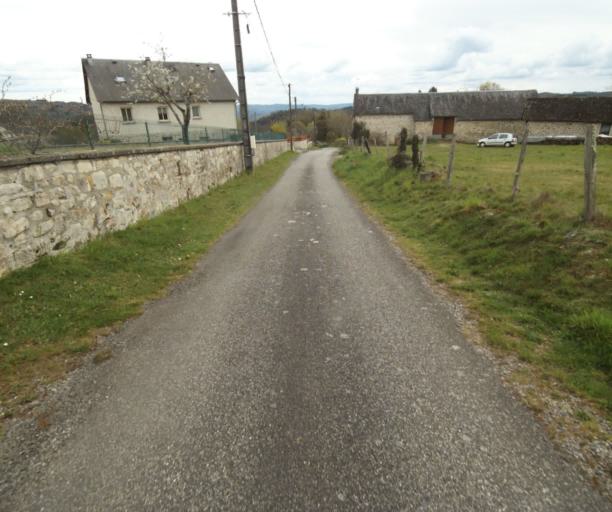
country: FR
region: Limousin
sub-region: Departement de la Correze
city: Argentat
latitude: 45.1897
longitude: 1.9534
